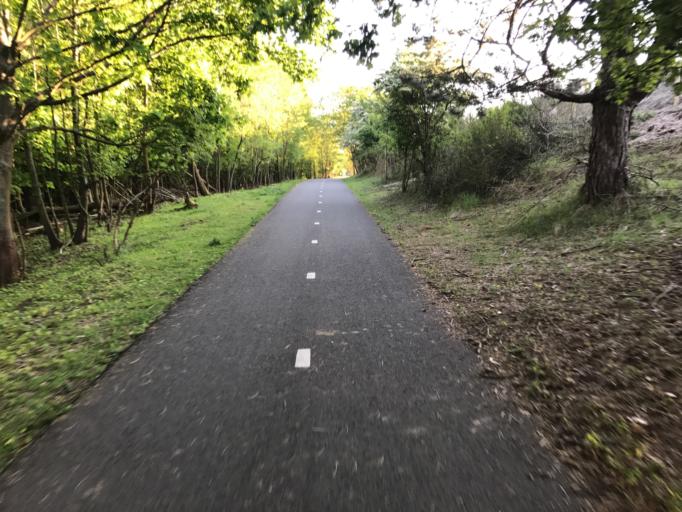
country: NL
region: South Holland
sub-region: Gemeente Noordwijkerhout
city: Noordwijkerhout
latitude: 52.2941
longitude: 4.4935
